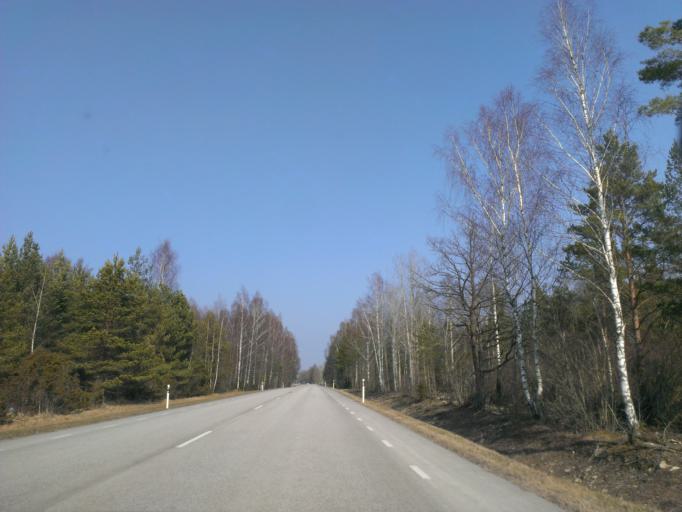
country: EE
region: Saare
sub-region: Orissaare vald
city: Orissaare
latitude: 58.5431
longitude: 23.0539
